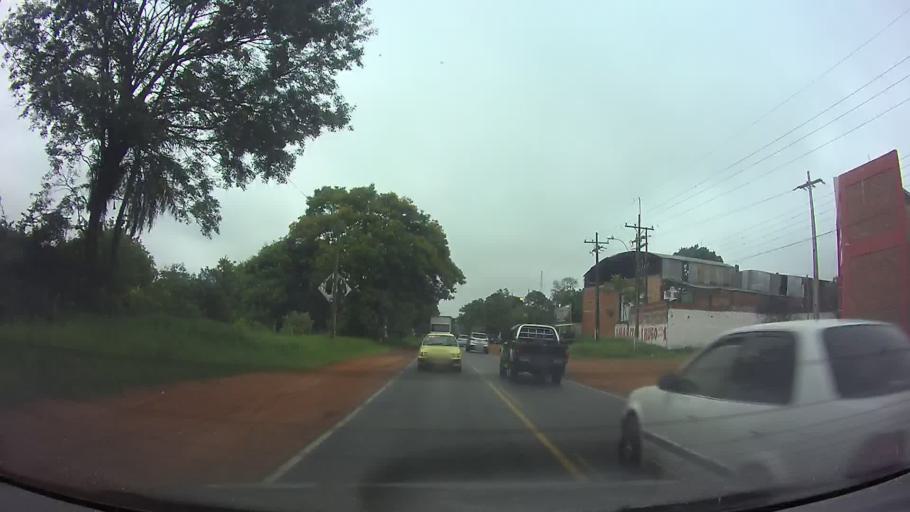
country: PY
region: Central
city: Itaugua
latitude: -25.4101
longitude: -57.3599
